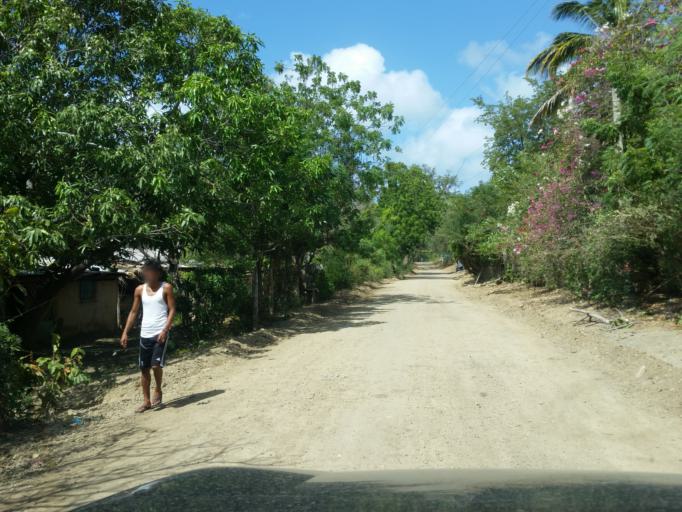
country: CR
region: Guanacaste
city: La Cruz
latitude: 11.1139
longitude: -85.7616
